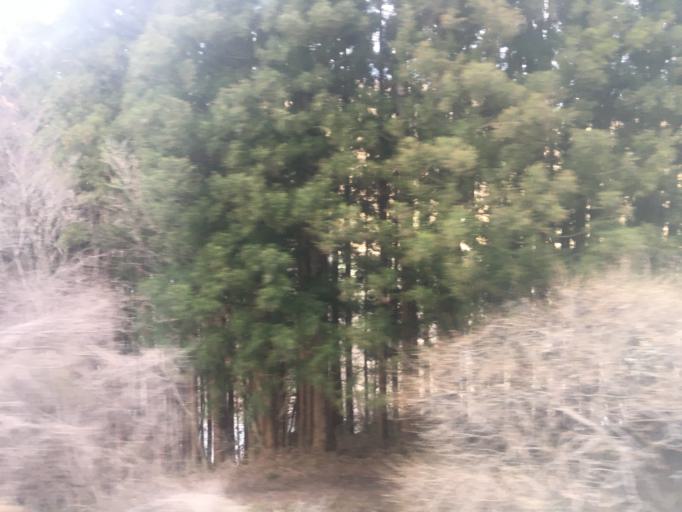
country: JP
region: Fukushima
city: Funehikimachi-funehiki
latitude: 37.2311
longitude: 140.7005
